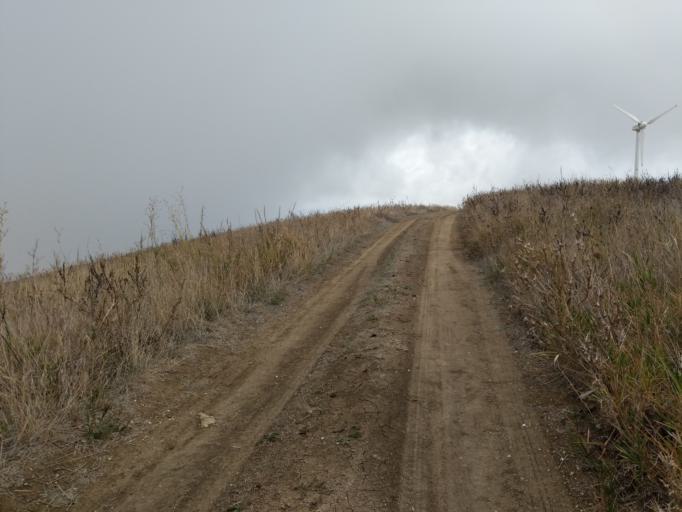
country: IT
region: Sicily
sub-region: Agrigento
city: Comitini
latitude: 37.4075
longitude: 13.6656
